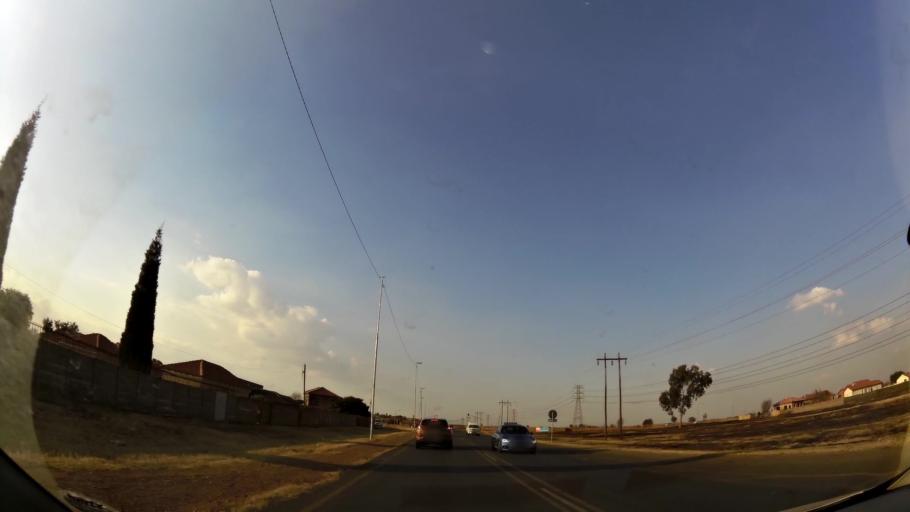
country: ZA
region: Gauteng
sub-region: Ekurhuleni Metropolitan Municipality
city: Boksburg
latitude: -26.3187
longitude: 28.2490
